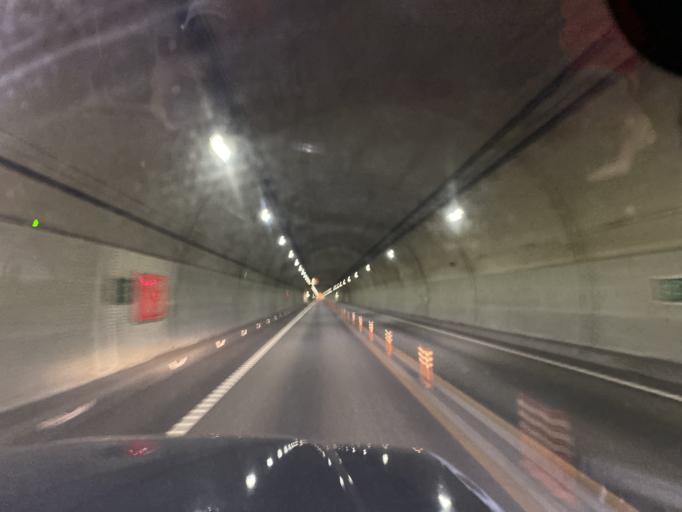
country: JP
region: Toyama
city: Fukumitsu
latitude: 36.3018
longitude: 136.9004
